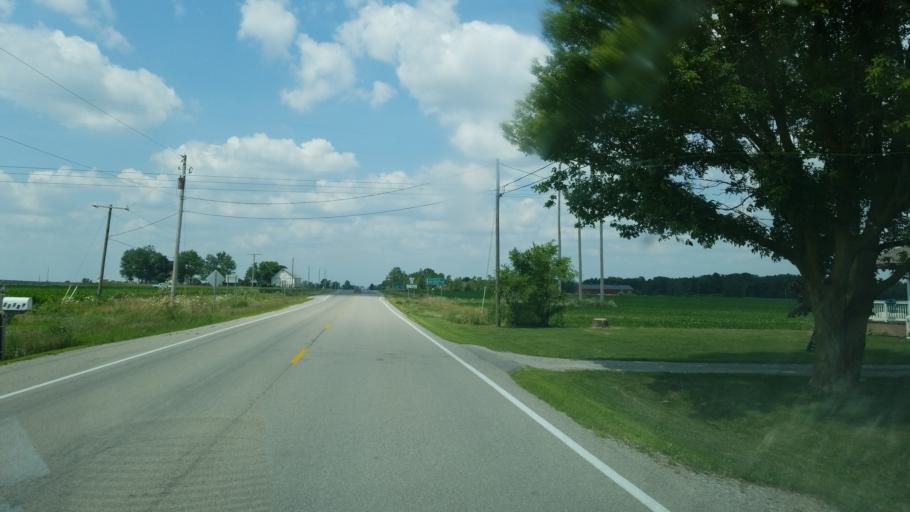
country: US
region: Ohio
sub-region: Defiance County
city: Defiance
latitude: 41.2824
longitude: -84.2895
